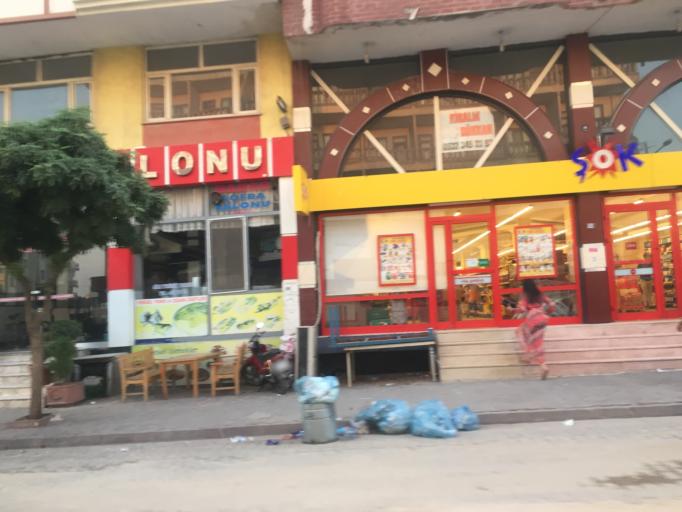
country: TR
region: Mardin
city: Midyat
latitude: 37.4250
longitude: 41.3391
